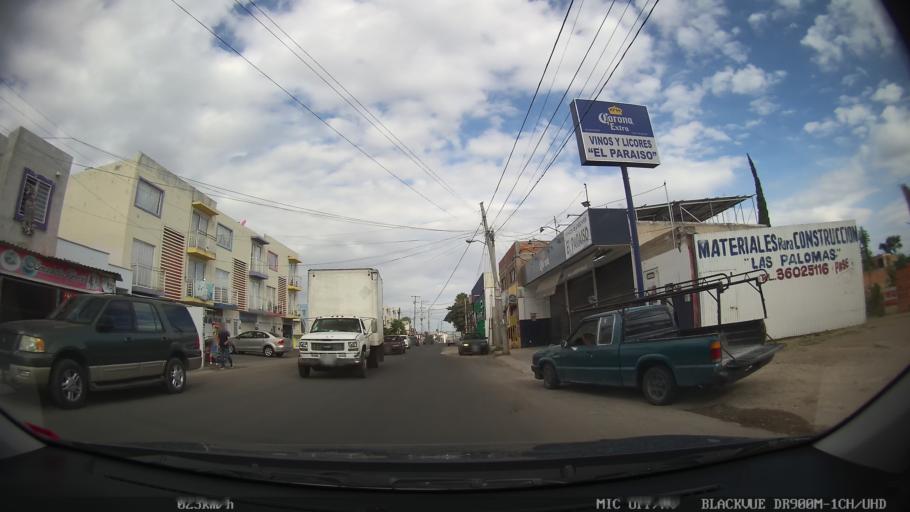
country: MX
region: Jalisco
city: Tonala
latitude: 20.6622
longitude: -103.2367
